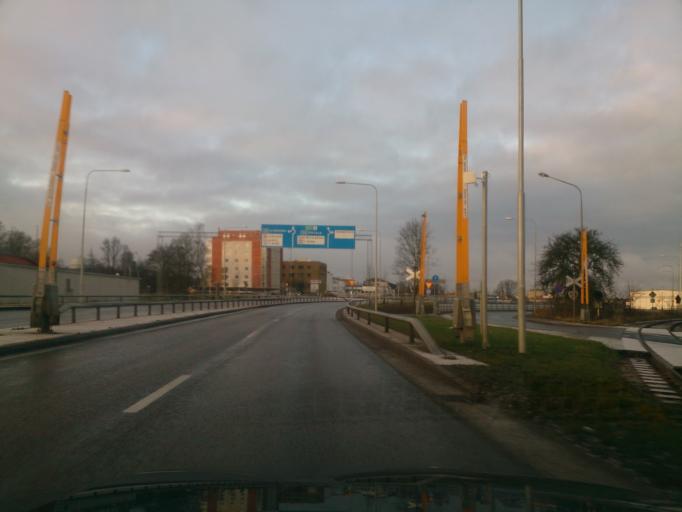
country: SE
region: OEstergoetland
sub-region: Linkopings Kommun
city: Linkoping
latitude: 58.4009
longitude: 15.6554
